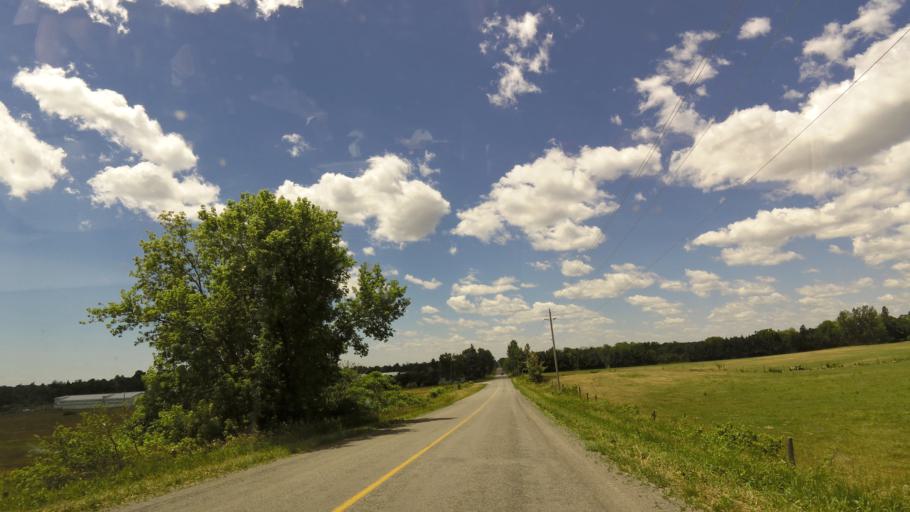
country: CA
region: Ontario
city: Oshawa
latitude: 43.9615
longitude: -78.5658
